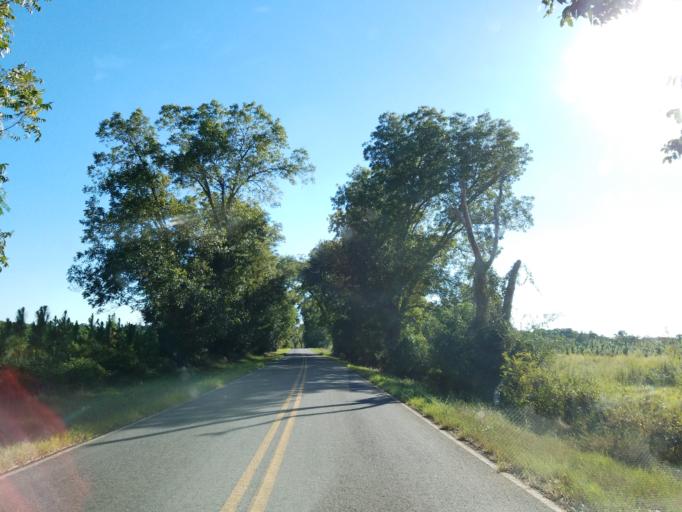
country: US
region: Georgia
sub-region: Dooly County
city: Vienna
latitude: 32.2090
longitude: -83.8979
